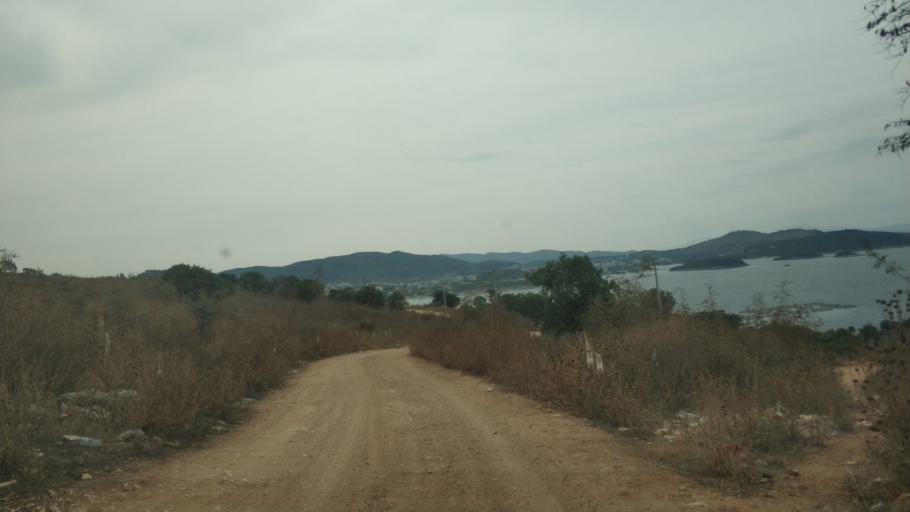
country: AL
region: Vlore
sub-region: Rrethi i Sarandes
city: Sarande
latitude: 39.7963
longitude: 20.0032
